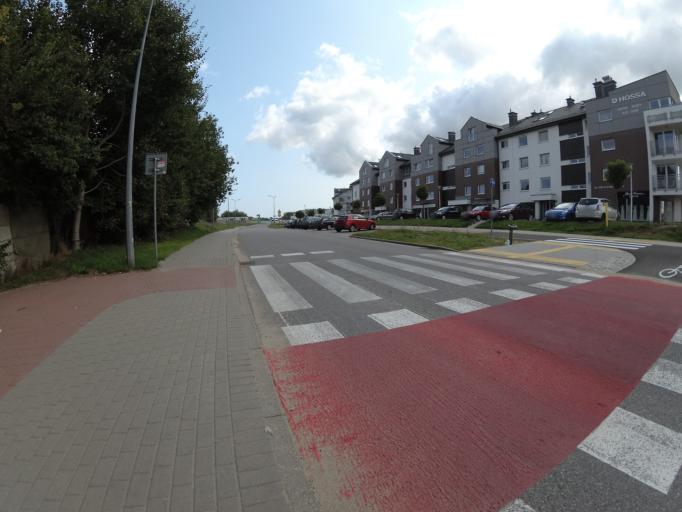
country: PL
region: Pomeranian Voivodeship
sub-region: Powiat wejherowski
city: Bojano
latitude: 54.4940
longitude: 18.4302
